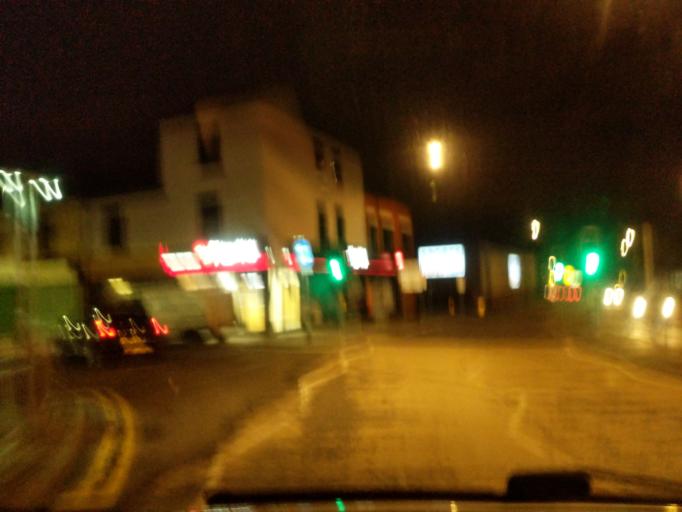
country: GB
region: England
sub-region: St. Helens
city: St Helens
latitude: 53.4548
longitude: -2.7392
